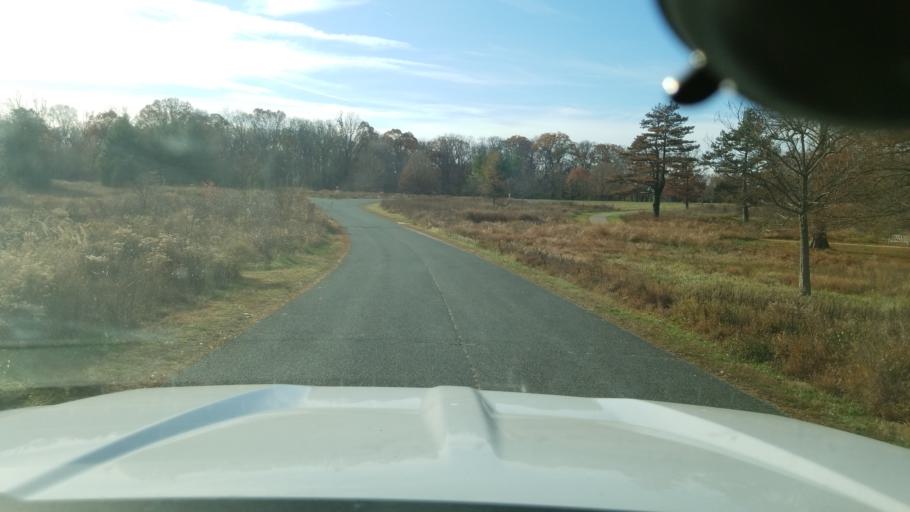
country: US
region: Maryland
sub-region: Prince George's County
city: Colmar Manor
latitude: 38.9095
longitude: -76.9668
